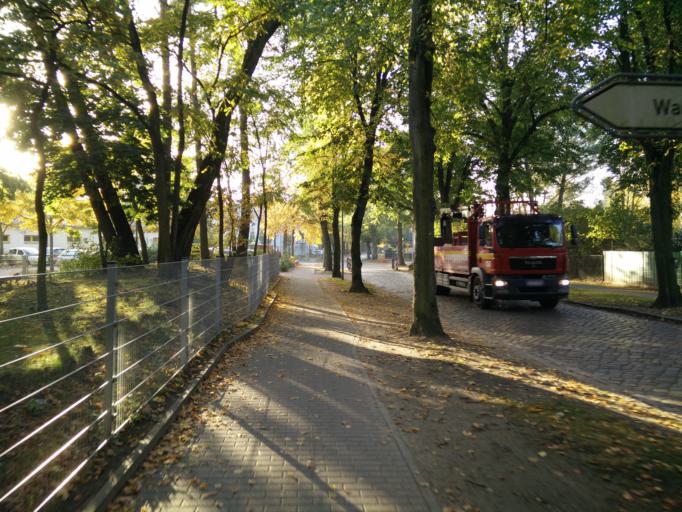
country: DE
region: Brandenburg
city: Falkensee
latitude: 52.5744
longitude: 13.0909
